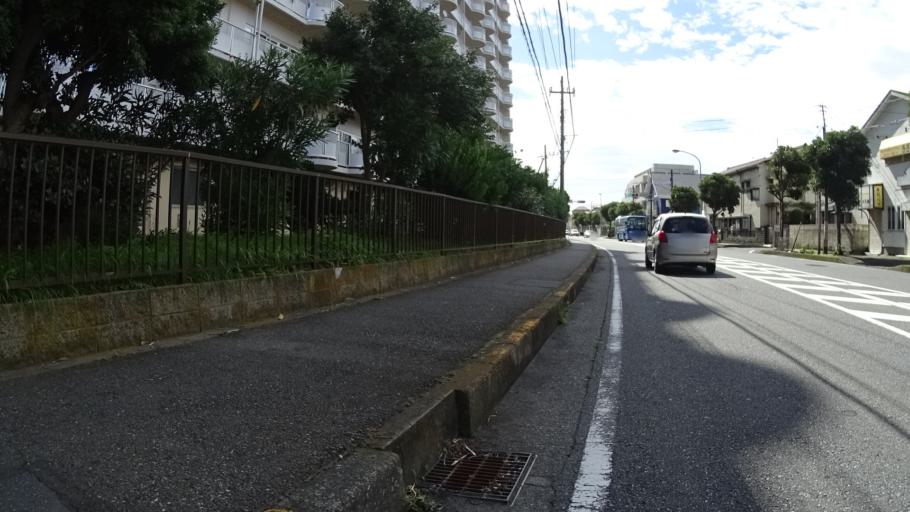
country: JP
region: Kanagawa
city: Yokosuka
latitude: 35.2629
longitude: 139.6952
